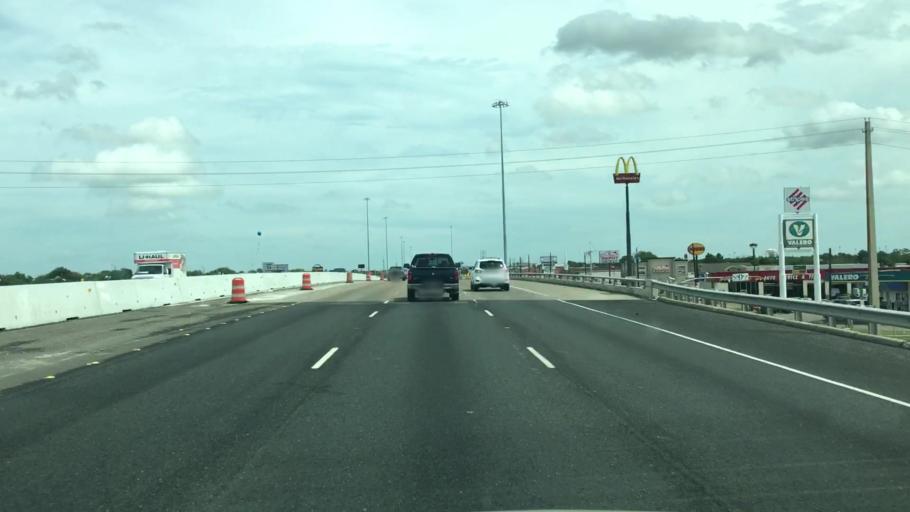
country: US
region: Texas
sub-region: Nueces County
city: Corpus Christi
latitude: 27.7288
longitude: -97.4135
